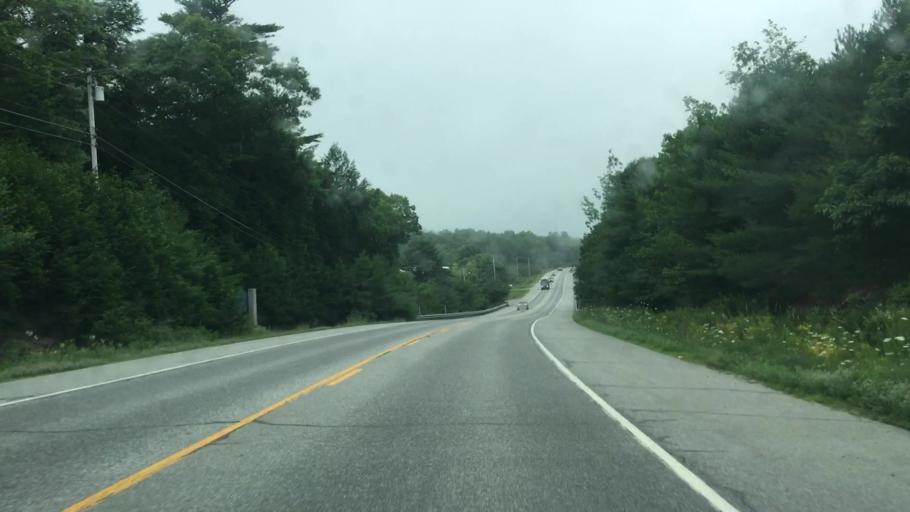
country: US
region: Maine
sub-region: Lincoln County
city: Edgecomb
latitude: 43.9389
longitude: -69.6249
